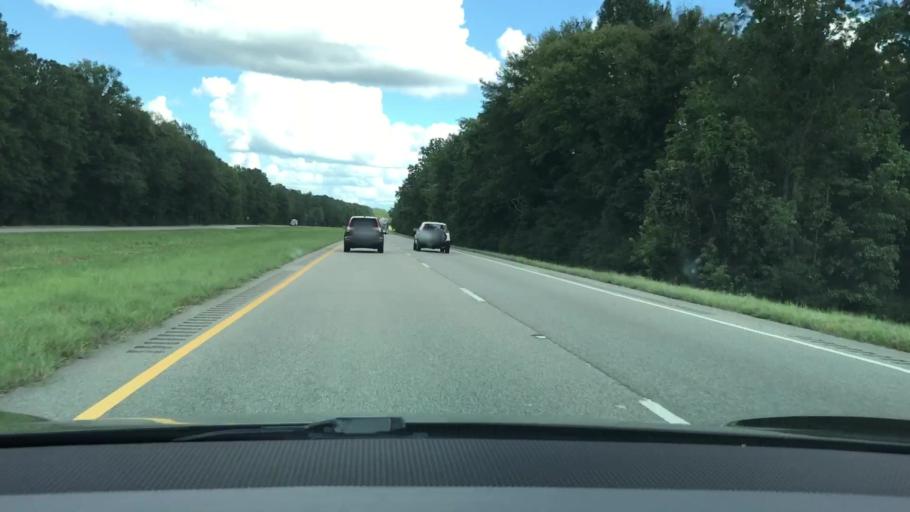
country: US
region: Alabama
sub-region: Montgomery County
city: Pike Road
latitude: 32.1390
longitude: -86.0940
